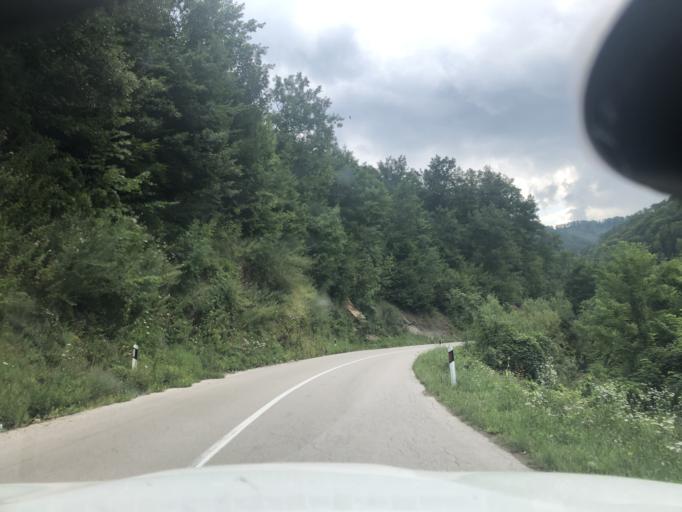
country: RS
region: Central Serbia
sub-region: Jablanicki Okrug
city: Medvega
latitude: 42.7863
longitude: 21.5873
